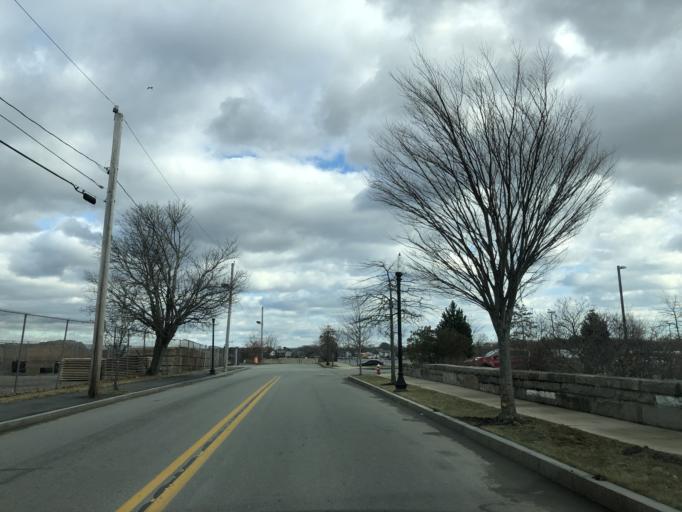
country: US
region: Massachusetts
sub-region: Bristol County
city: New Bedford
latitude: 41.6584
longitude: -70.9211
